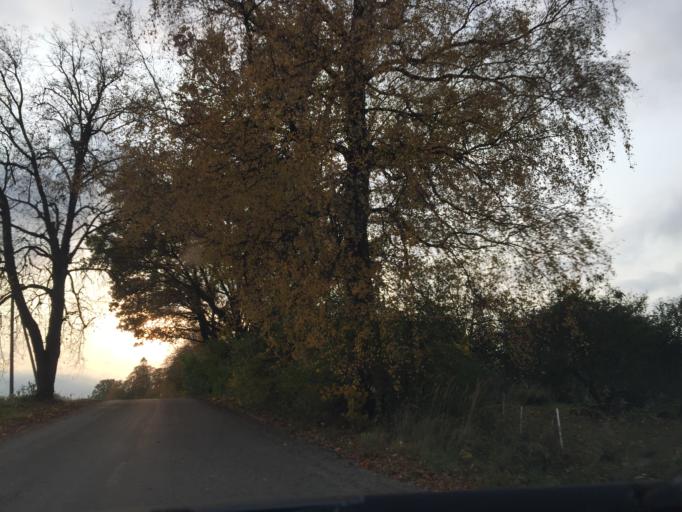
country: LV
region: Pargaujas
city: Stalbe
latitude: 57.3344
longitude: 25.1377
